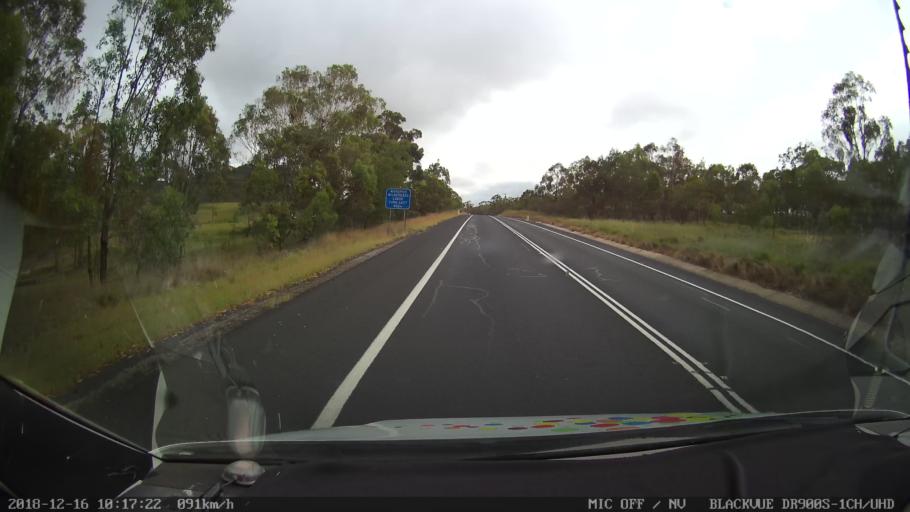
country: AU
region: New South Wales
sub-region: Tenterfield Municipality
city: Carrolls Creek
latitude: -29.2565
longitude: 151.9911
